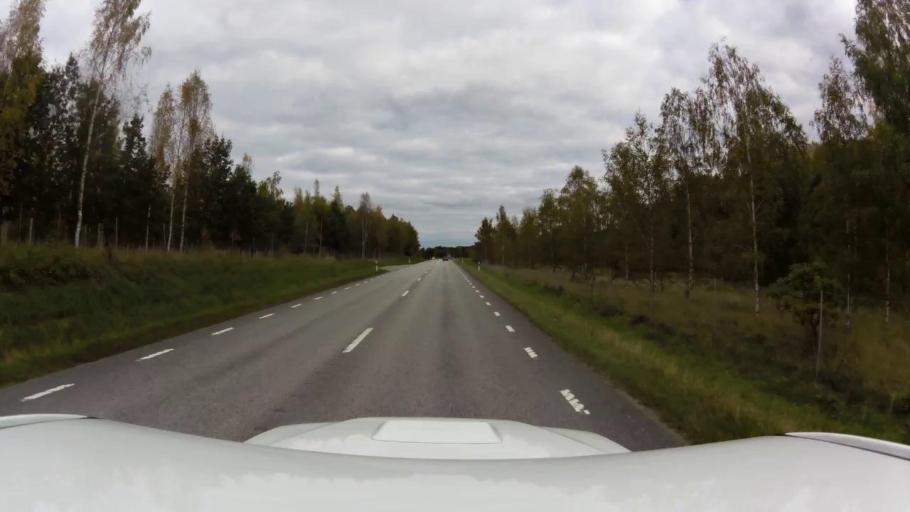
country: SE
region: OEstergoetland
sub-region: Kinda Kommun
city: Rimforsa
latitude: 58.2044
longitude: 15.6685
